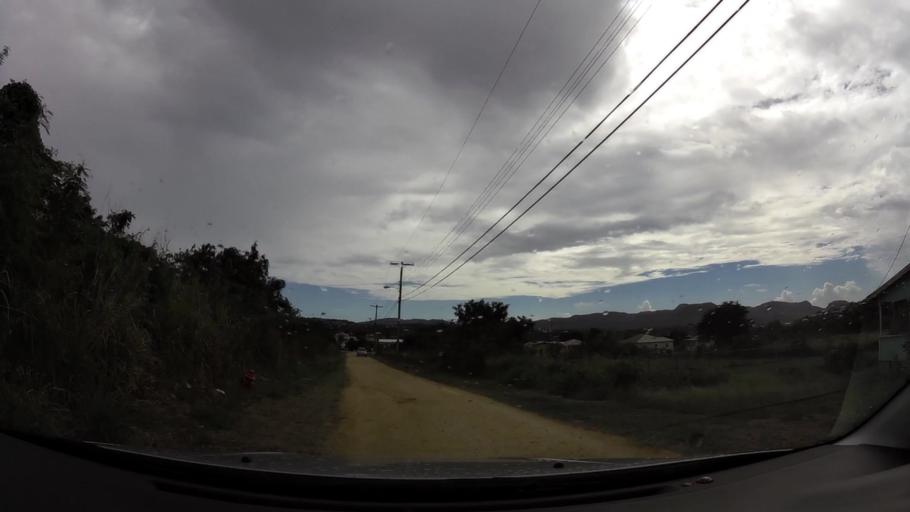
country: AG
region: Saint John
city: Potters Village
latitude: 17.0956
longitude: -61.8154
